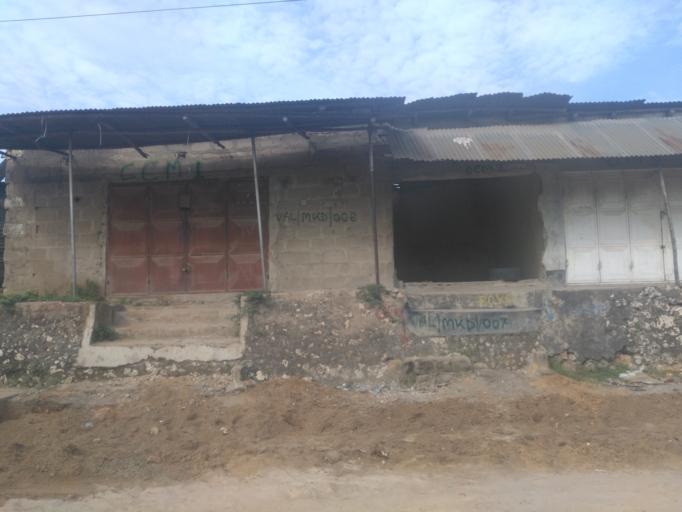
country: TZ
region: Zanzibar Urban/West
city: Zanzibar
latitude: -6.1598
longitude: 39.2095
